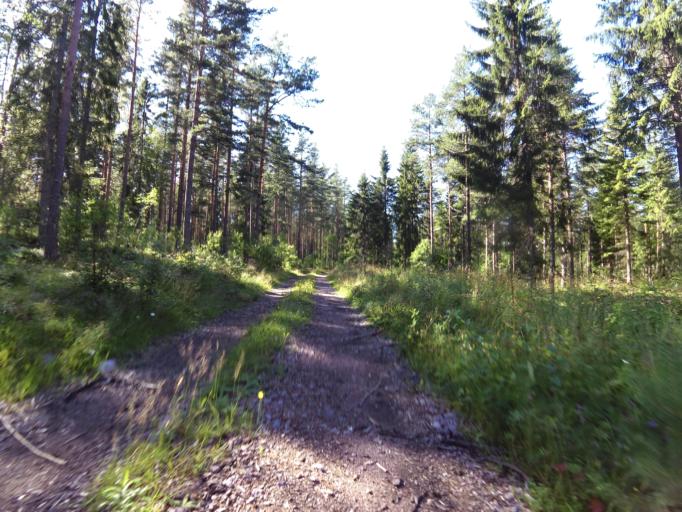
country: SE
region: Gaevleborg
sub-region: Hofors Kommun
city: Hofors
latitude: 60.5653
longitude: 16.4750
